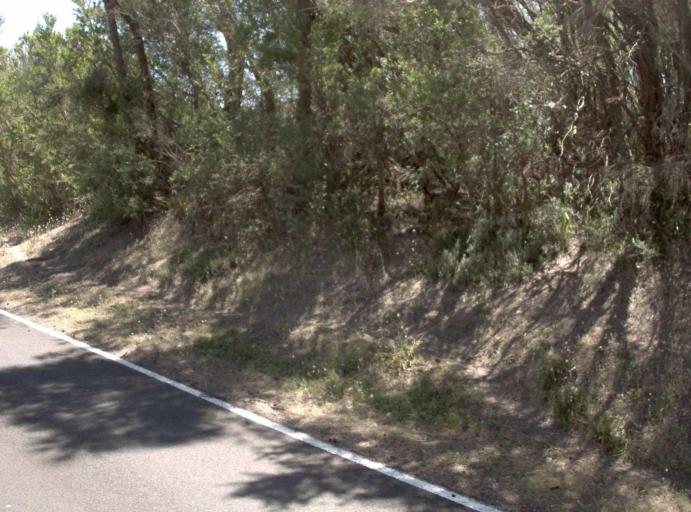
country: AU
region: Victoria
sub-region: Latrobe
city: Morwell
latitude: -38.8605
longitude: 146.2532
